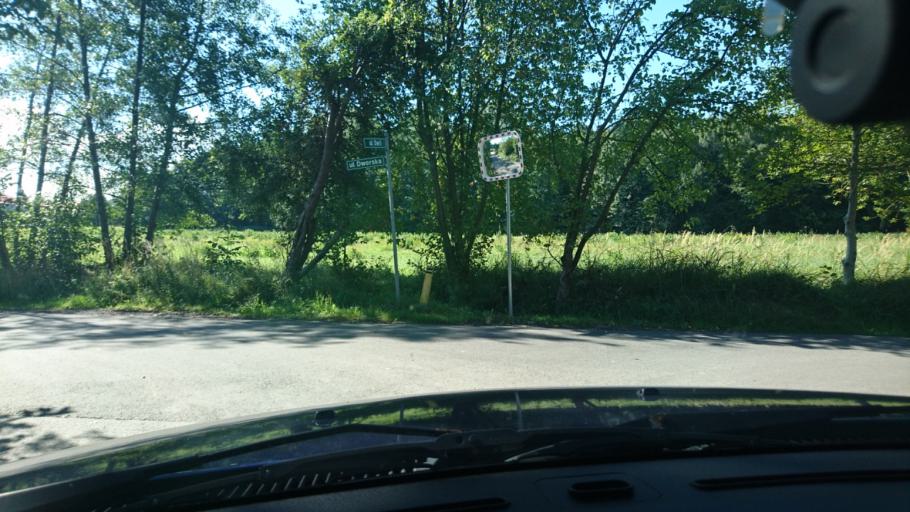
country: PL
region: Silesian Voivodeship
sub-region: Powiat bielski
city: Jaworze
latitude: 49.8187
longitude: 18.9665
